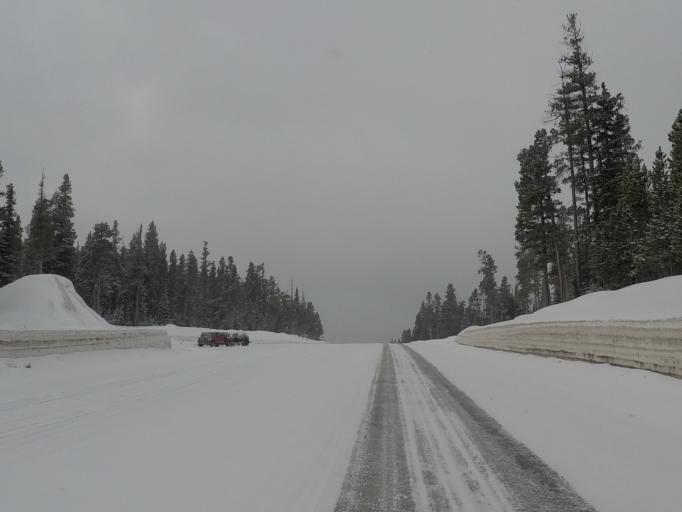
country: US
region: Montana
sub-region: Meagher County
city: White Sulphur Springs
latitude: 46.8419
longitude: -110.6945
